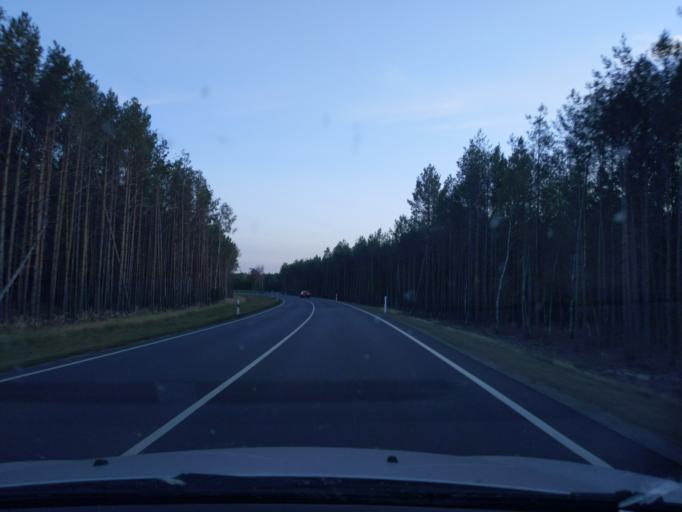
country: DE
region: Saxony
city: Wittichenau
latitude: 51.4121
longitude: 14.2900
